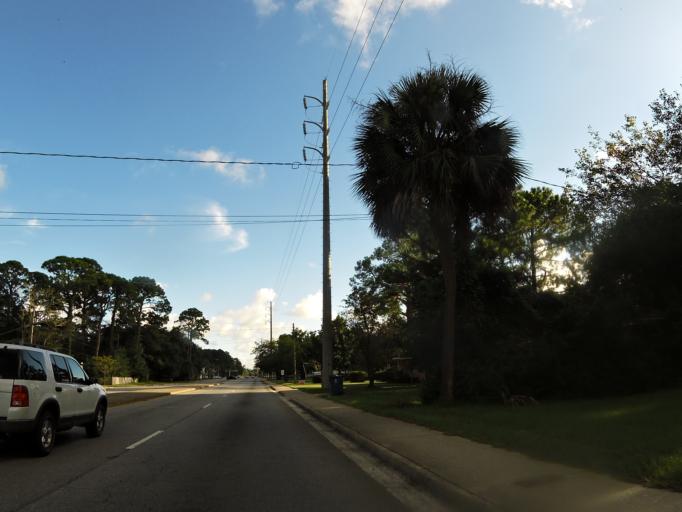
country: US
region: Georgia
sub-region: Glynn County
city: Brunswick
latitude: 31.1769
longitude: -81.4905
